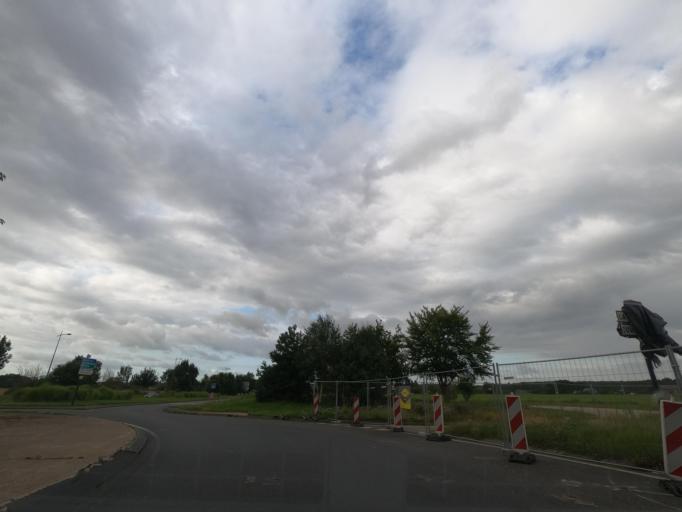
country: FR
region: Haute-Normandie
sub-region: Departement de l'Eure
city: Bourgtheroulde-Infreville
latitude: 49.3027
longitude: 0.8835
